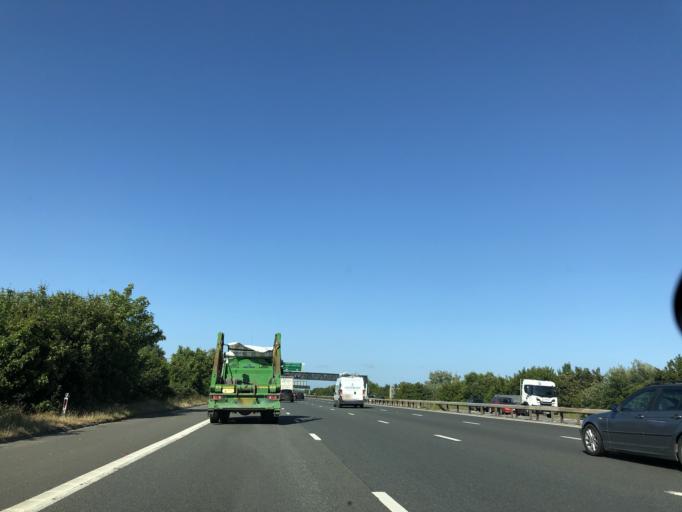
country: GB
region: England
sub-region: Portsmouth
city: Cosham
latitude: 50.8382
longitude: -1.0311
